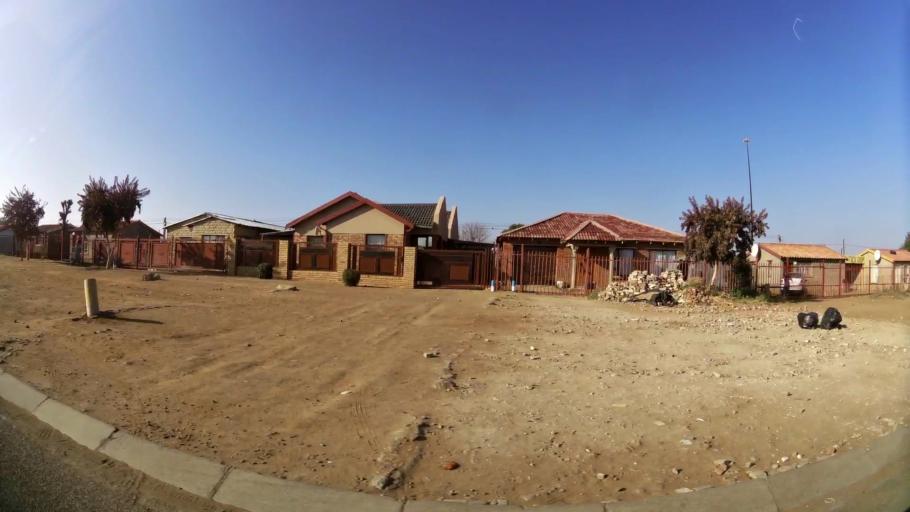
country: ZA
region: Orange Free State
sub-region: Mangaung Metropolitan Municipality
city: Bloemfontein
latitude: -29.2012
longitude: 26.2210
